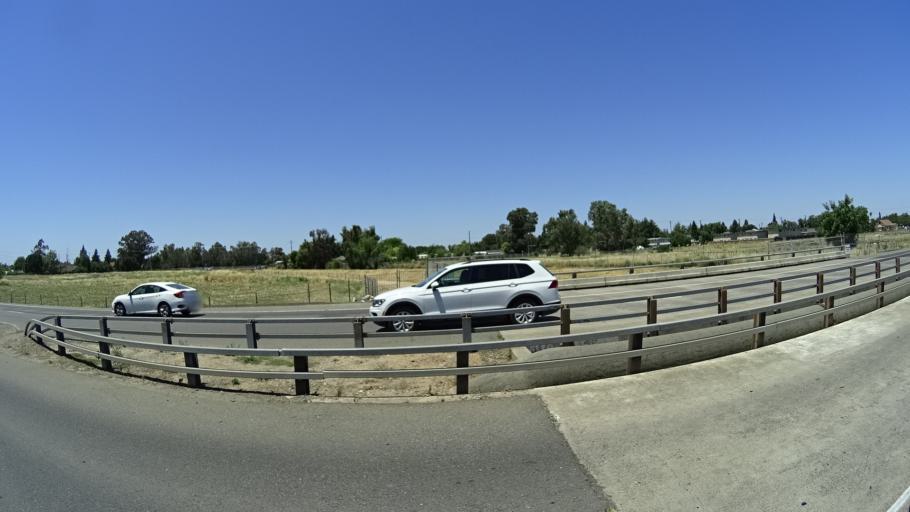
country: US
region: California
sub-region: Sacramento County
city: Florin
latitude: 38.5137
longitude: -121.4274
